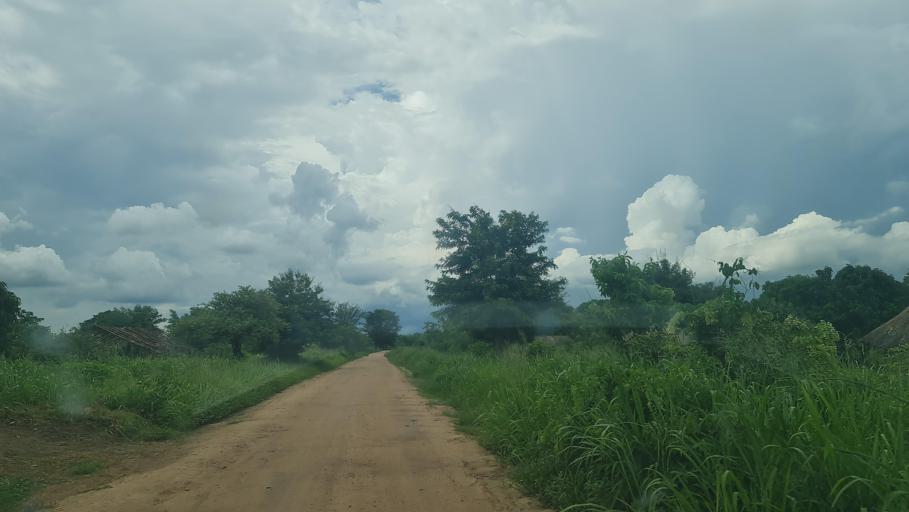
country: MW
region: Southern Region
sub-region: Nsanje District
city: Nsanje
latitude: -17.5981
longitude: 35.6758
